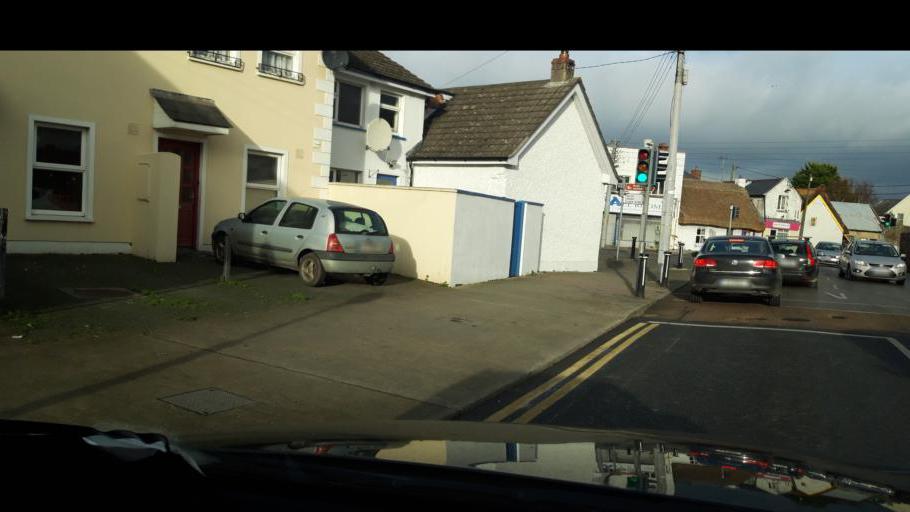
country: IE
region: Leinster
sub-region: Fingal County
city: Skerries
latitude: 53.5798
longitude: -6.1102
